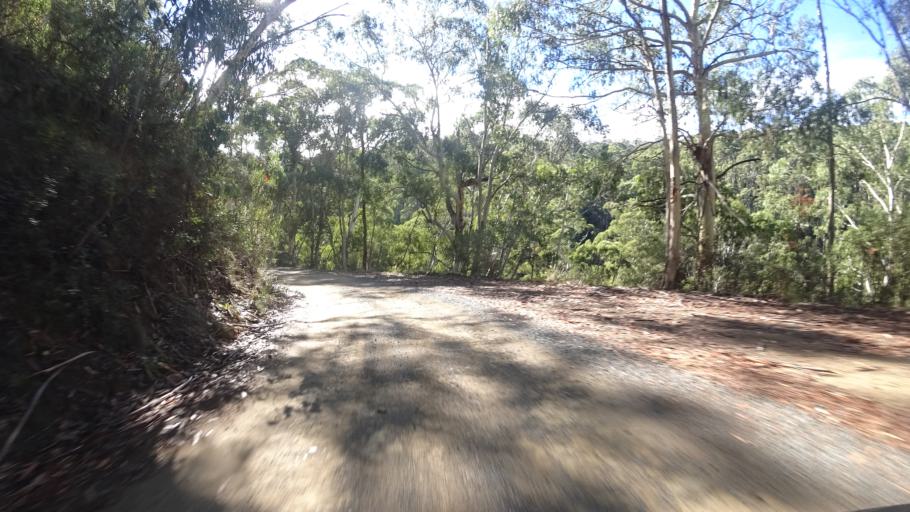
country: AU
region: New South Wales
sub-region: Tumut Shire
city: Tumut
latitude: -35.7244
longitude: 148.4999
